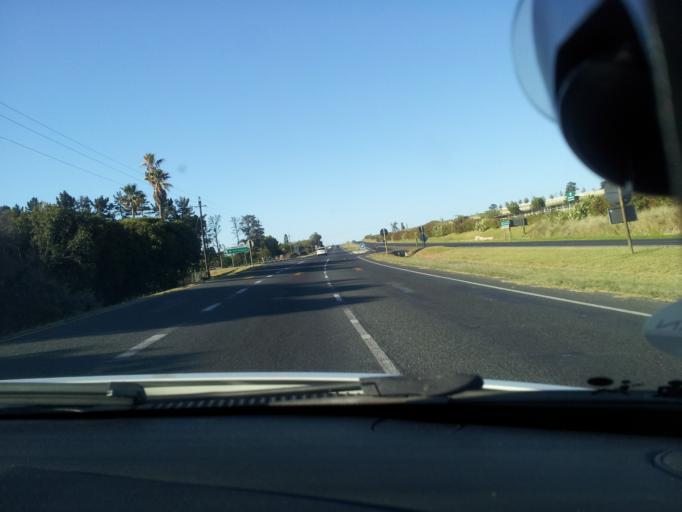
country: ZA
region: Western Cape
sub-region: Cape Winelands District Municipality
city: Stellenbosch
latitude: -34.0258
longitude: 18.8199
